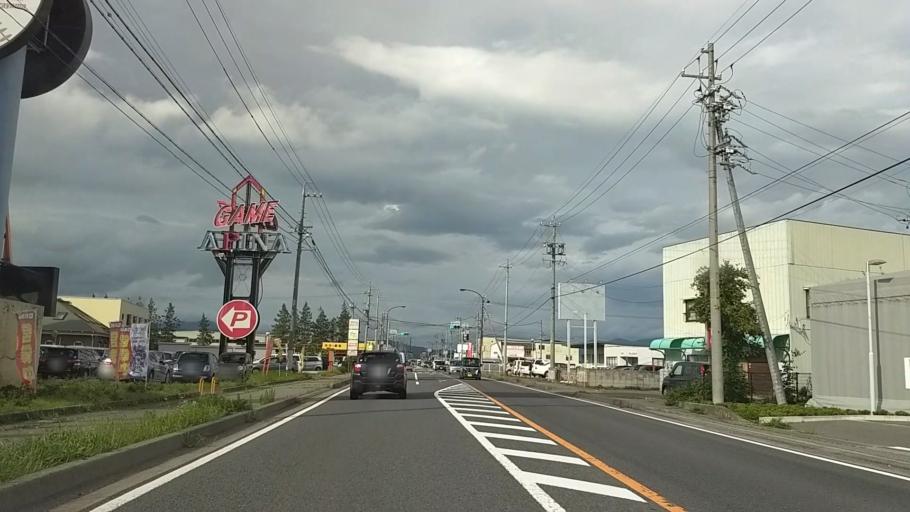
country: JP
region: Nagano
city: Suzaka
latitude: 36.6674
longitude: 138.2637
